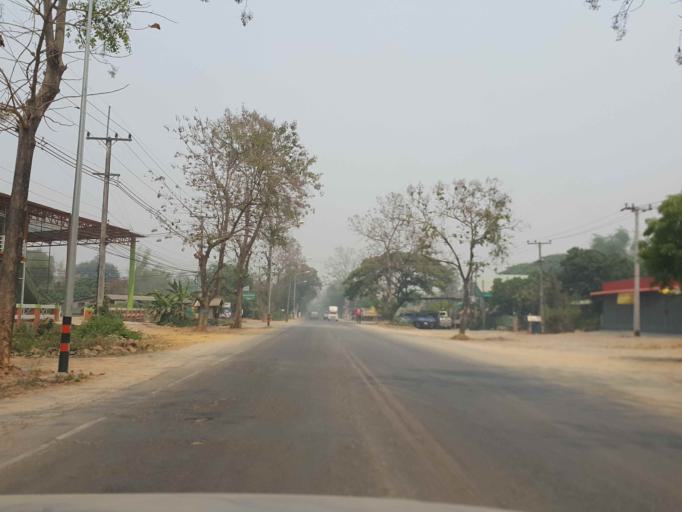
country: TH
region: Chiang Mai
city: Mae Taeng
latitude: 18.9931
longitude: 98.9781
